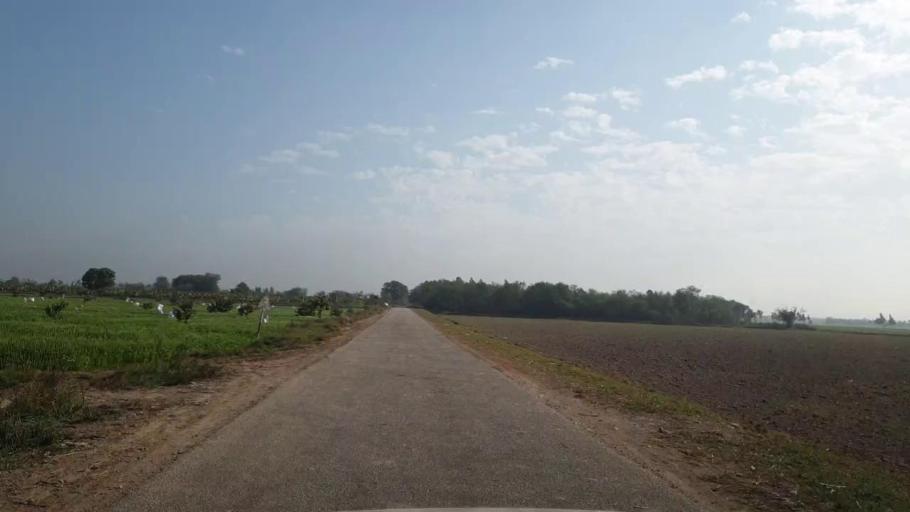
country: PK
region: Sindh
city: Matiari
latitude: 25.5995
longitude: 68.4955
